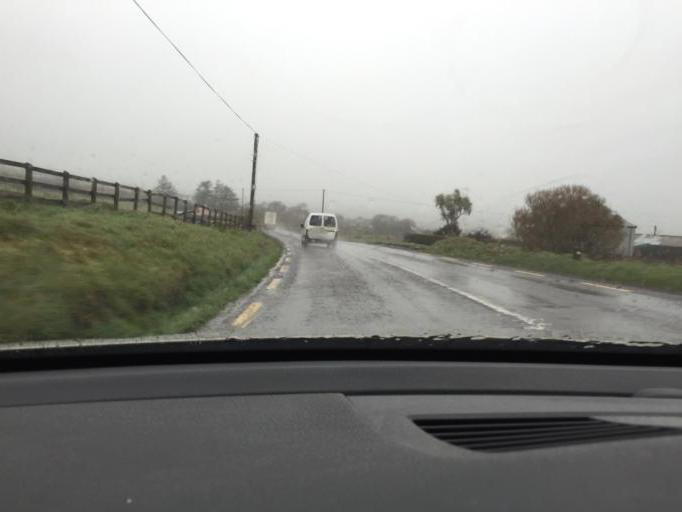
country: IE
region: Munster
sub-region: Ciarrai
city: Dingle
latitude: 52.1349
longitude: -10.2415
